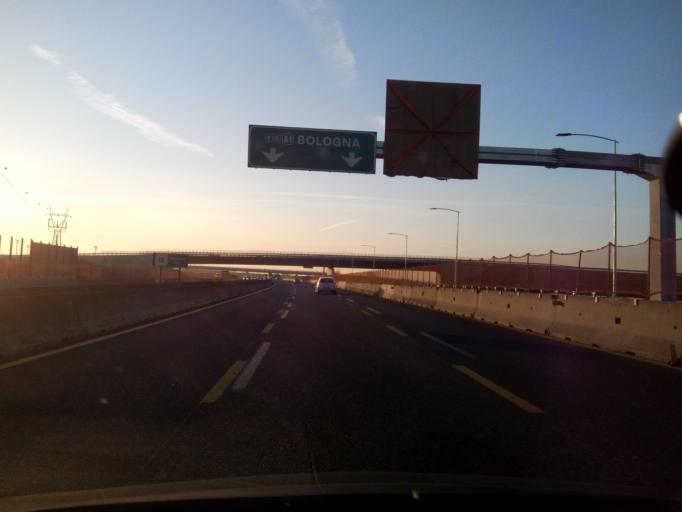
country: IT
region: Lombardy
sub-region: Citta metropolitana di Milano
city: Riozzo
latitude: 45.3421
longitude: 9.3192
